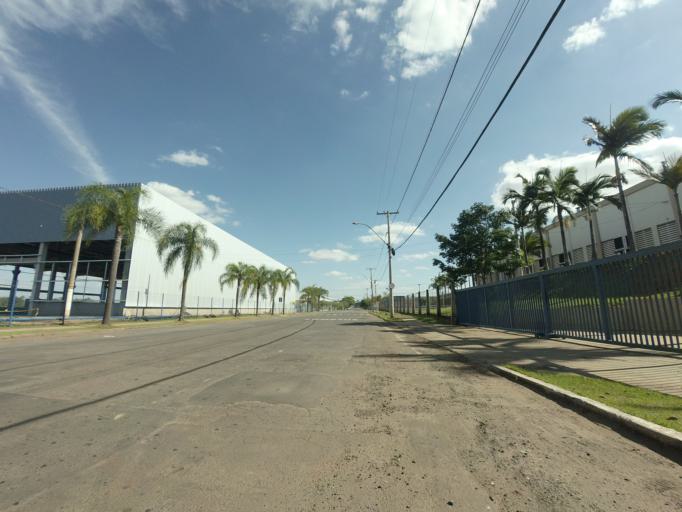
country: BR
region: Sao Paulo
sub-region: Piracicaba
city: Piracicaba
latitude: -22.7271
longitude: -47.5955
